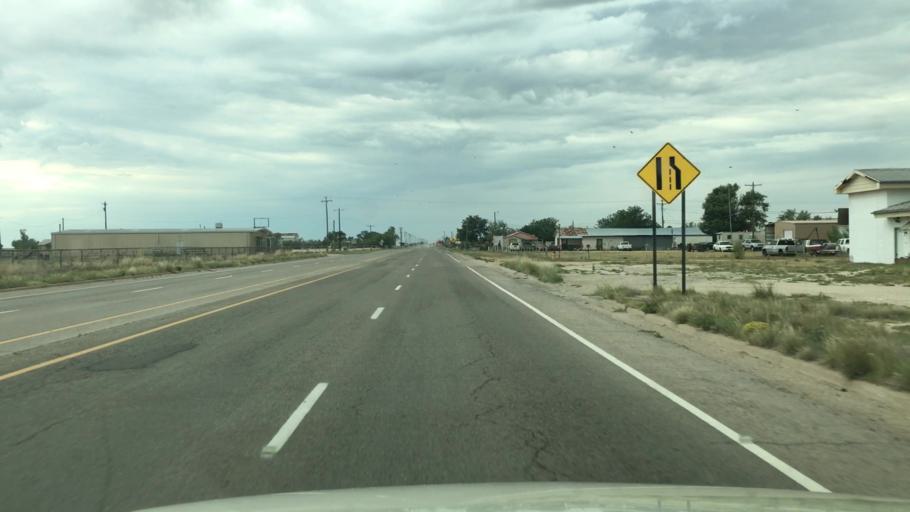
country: US
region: New Mexico
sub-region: Lea County
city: Lovington
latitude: 33.2570
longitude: -103.3331
